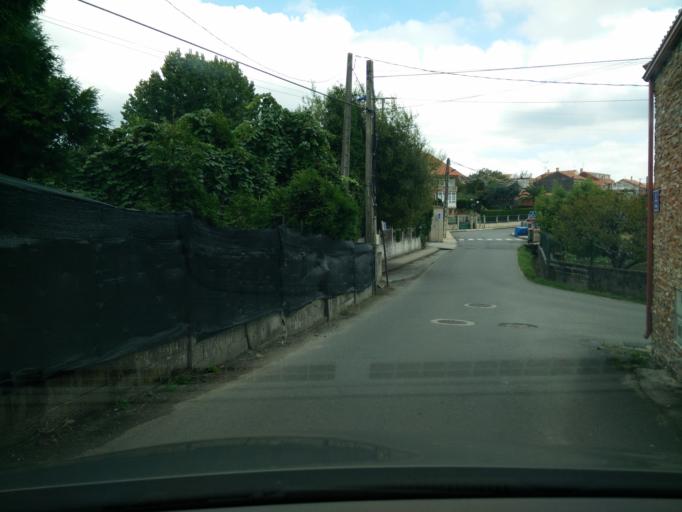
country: ES
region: Galicia
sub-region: Provincia da Coruna
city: Culleredo
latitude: 43.3138
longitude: -8.3908
